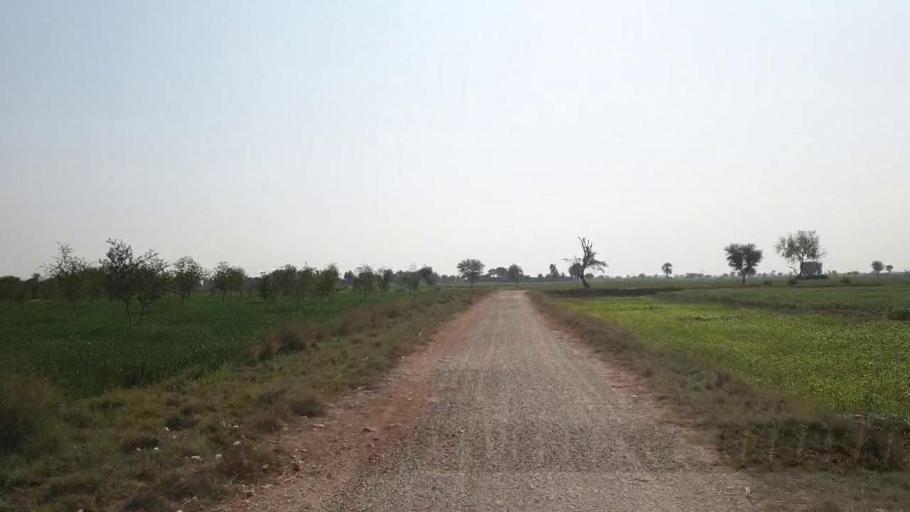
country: PK
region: Sindh
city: Shahdadpur
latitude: 25.9440
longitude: 68.4860
